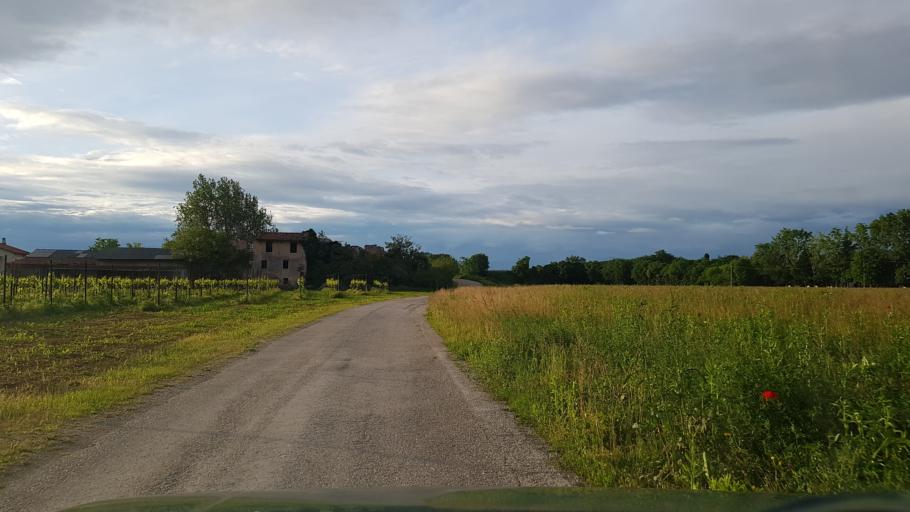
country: IT
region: Friuli Venezia Giulia
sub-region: Provincia di Gorizia
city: Sagrado
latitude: 45.8905
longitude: 13.4666
